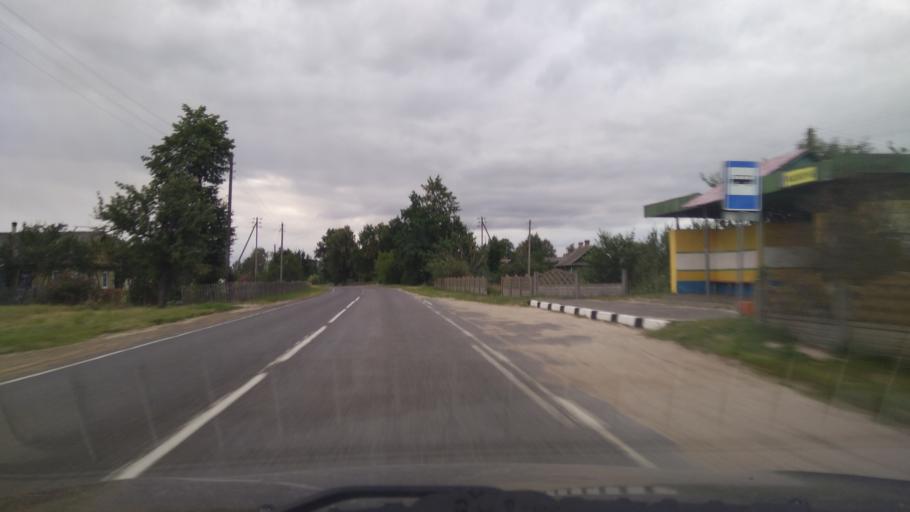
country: BY
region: Brest
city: Byaroza
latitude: 52.4224
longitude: 24.9810
